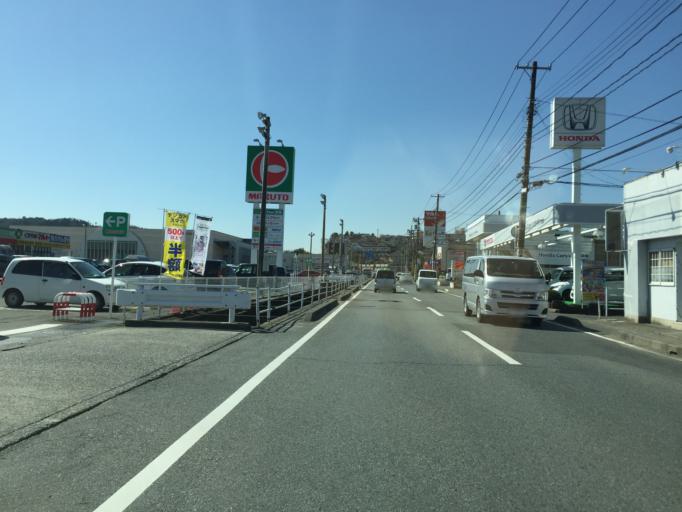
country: JP
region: Fukushima
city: Iwaki
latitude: 37.0449
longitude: 140.8616
